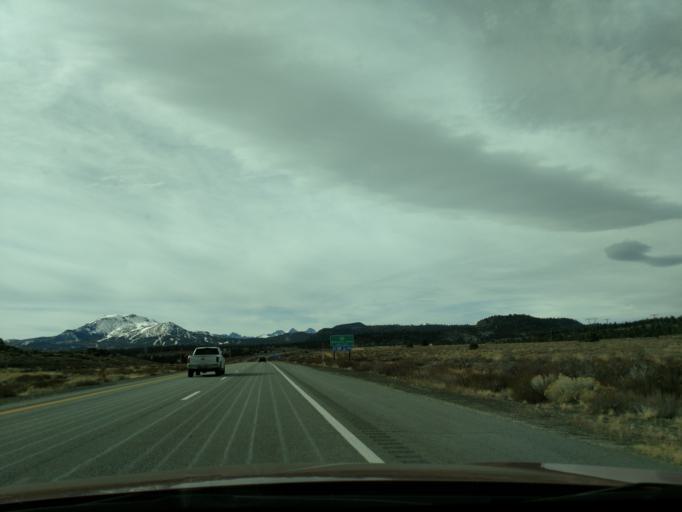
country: US
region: California
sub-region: Mono County
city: Mammoth Lakes
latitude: 37.6371
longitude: -118.8962
